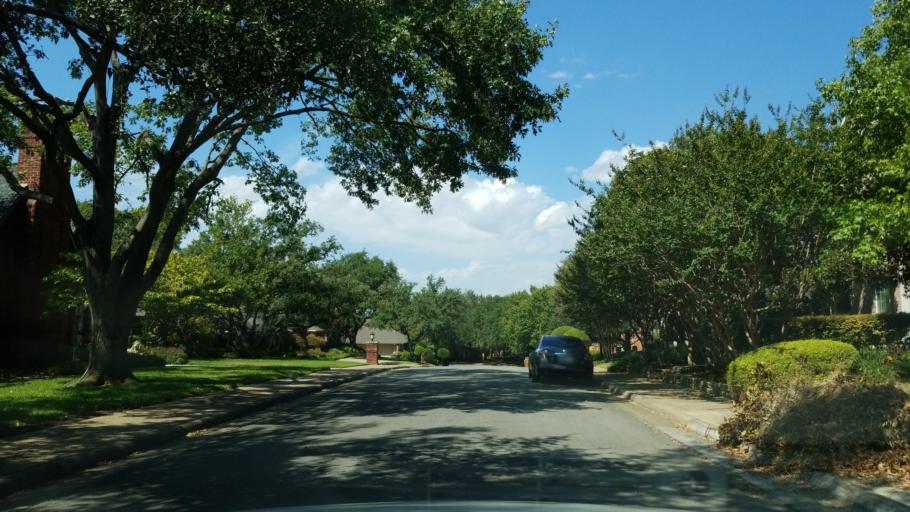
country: US
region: Texas
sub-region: Dallas County
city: Addison
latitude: 32.9692
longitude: -96.8005
